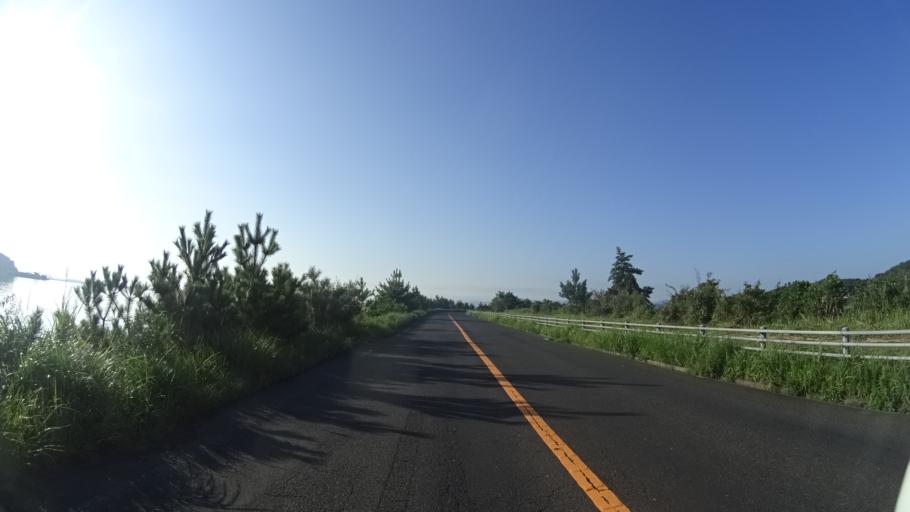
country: JP
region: Shimane
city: Sakaiminato
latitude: 35.5336
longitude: 133.1540
